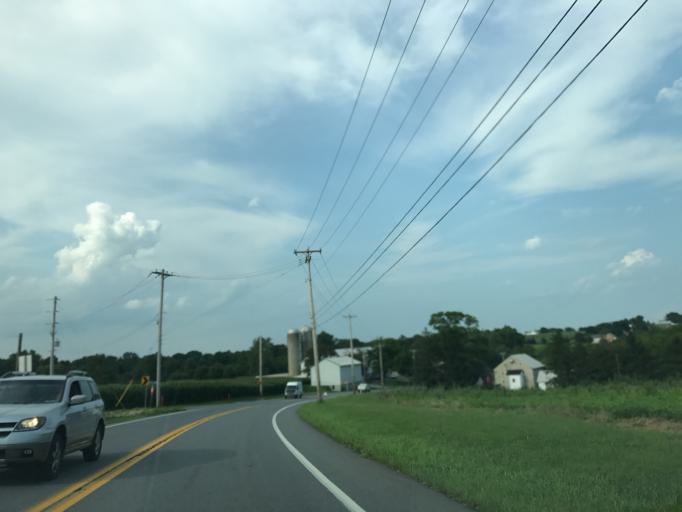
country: US
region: Pennsylvania
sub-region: Lancaster County
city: Marietta
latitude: 40.0775
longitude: -76.5376
